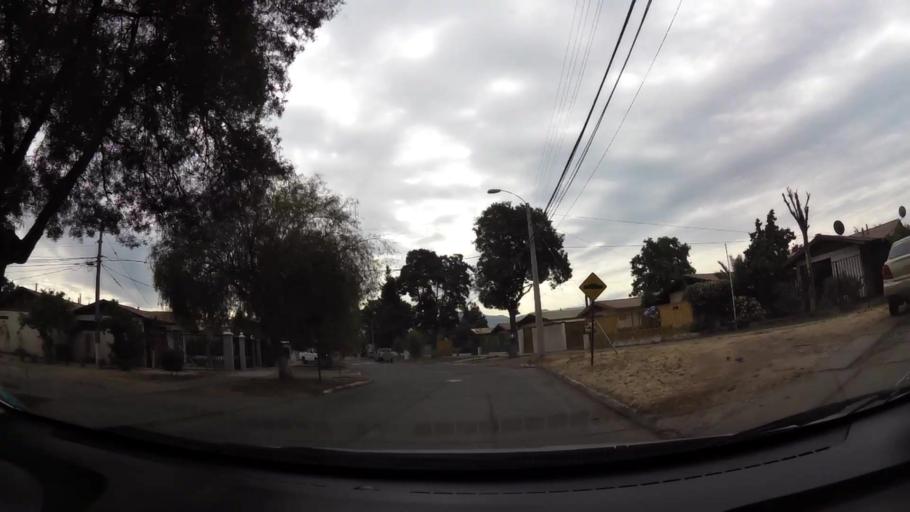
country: CL
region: O'Higgins
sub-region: Provincia de Cachapoal
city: Rancagua
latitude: -34.1626
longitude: -70.7428
